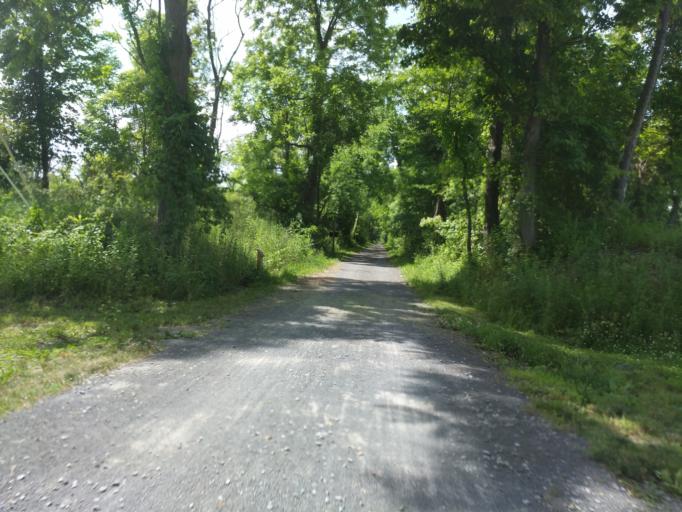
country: US
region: New York
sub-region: Tompkins County
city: Northwest Ithaca
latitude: 42.5133
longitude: -76.5620
